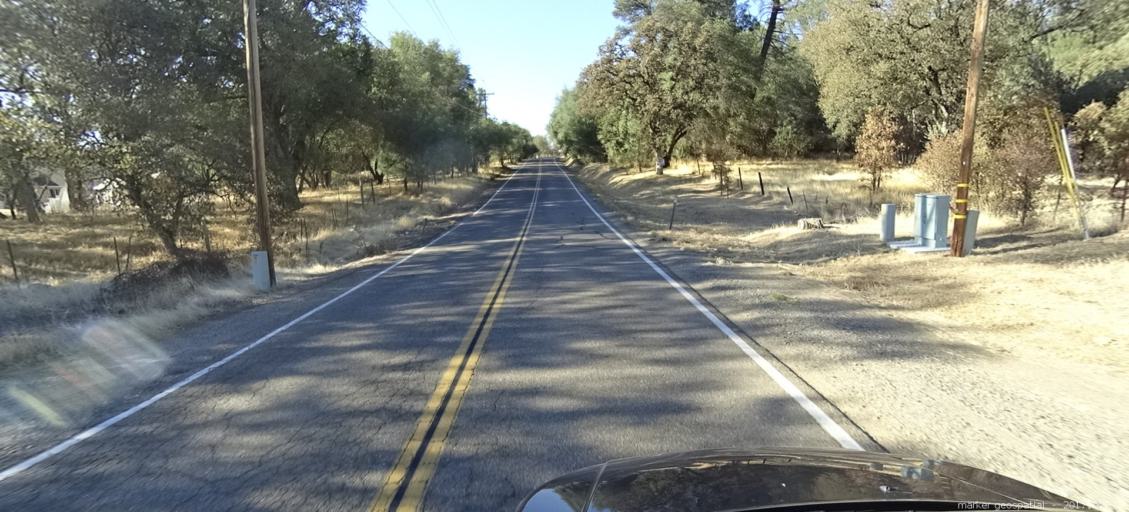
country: US
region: California
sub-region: Shasta County
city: Palo Cedro
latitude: 40.5572
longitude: -122.1857
